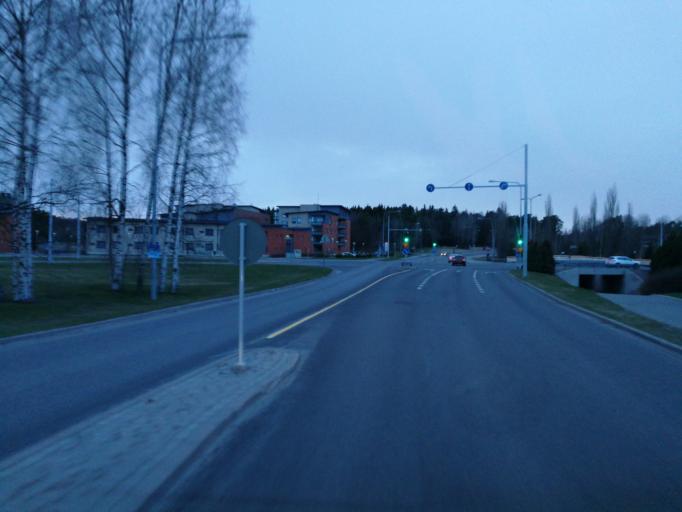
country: FI
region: Varsinais-Suomi
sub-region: Turku
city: Turku
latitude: 60.4735
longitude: 22.2343
